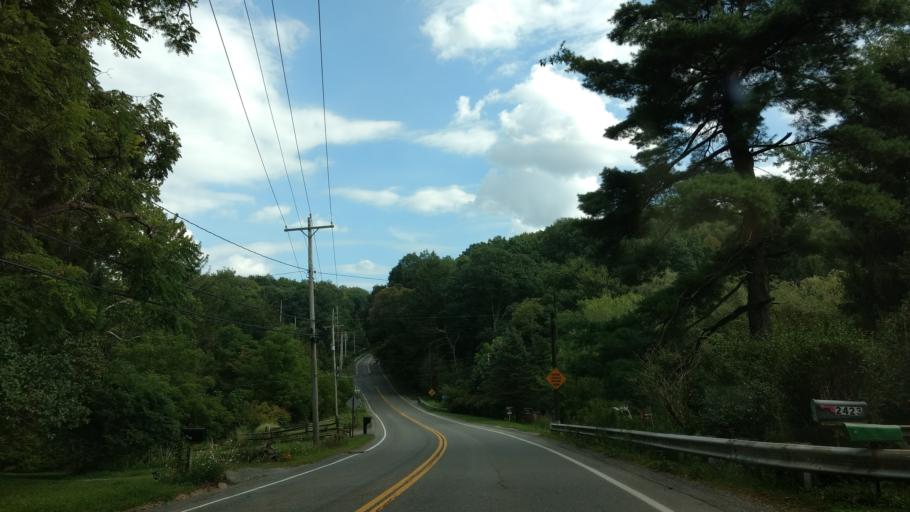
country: US
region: Pennsylvania
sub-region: Allegheny County
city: Franklin Park
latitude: 40.5932
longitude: -80.0765
